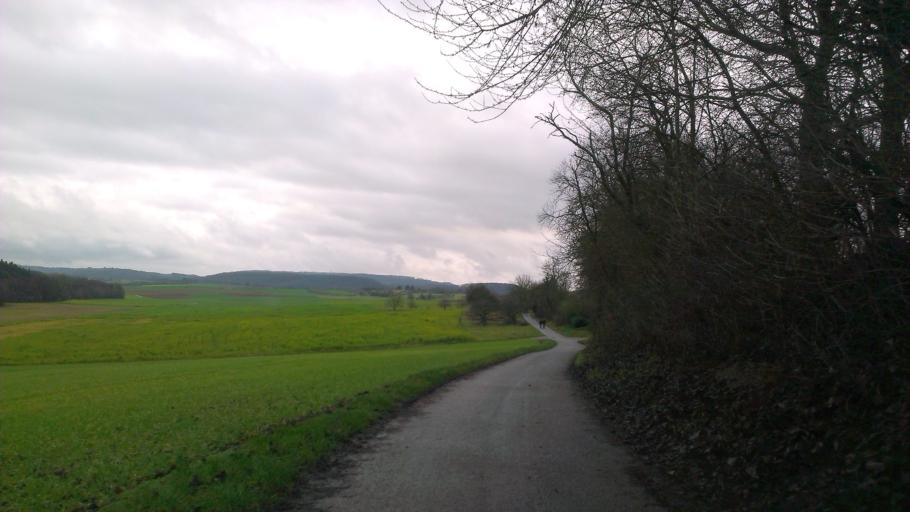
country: DE
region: Baden-Wuerttemberg
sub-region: Karlsruhe Region
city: Oberderdingen
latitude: 49.0831
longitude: 8.7901
